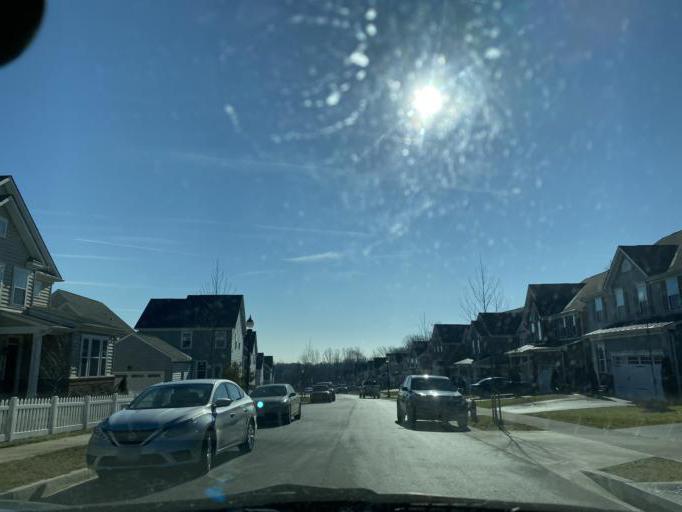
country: US
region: Maryland
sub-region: Montgomery County
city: Burtonsville
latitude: 39.0947
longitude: -76.9233
